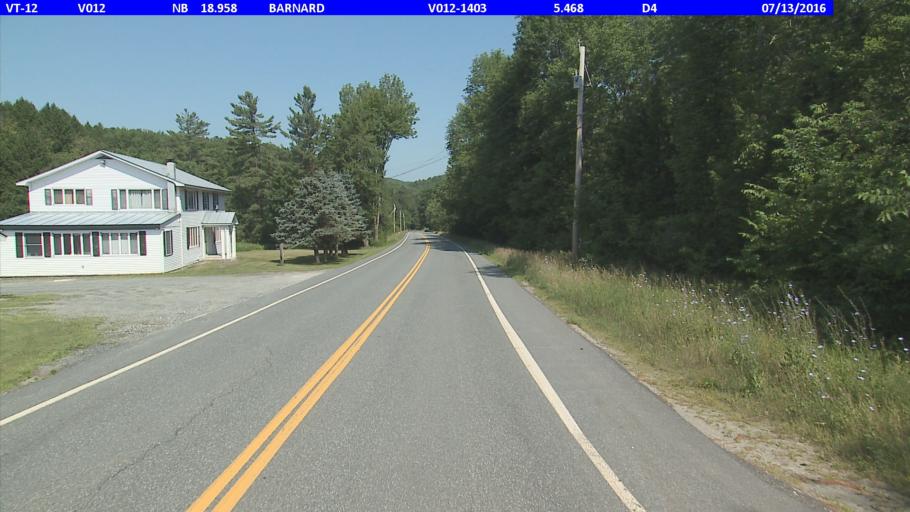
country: US
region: Vermont
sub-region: Windsor County
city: Woodstock
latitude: 43.7363
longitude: -72.6273
